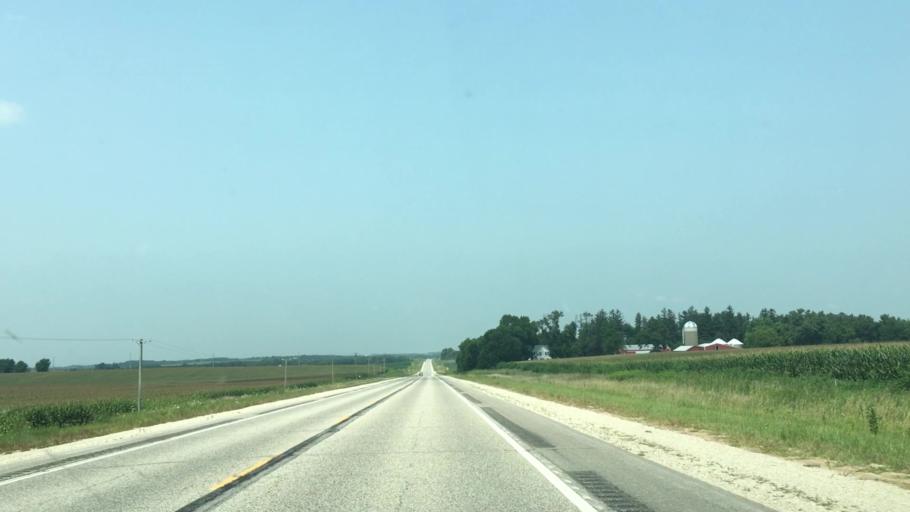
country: US
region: Iowa
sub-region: Fayette County
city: Fayette
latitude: 42.7815
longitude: -91.8047
